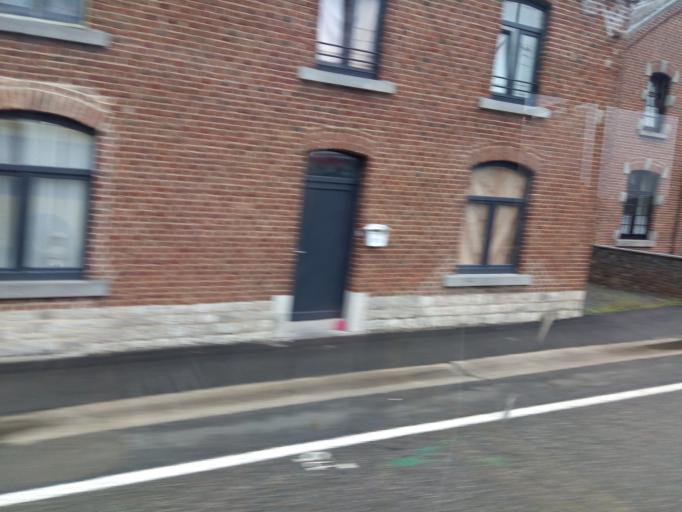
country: BE
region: Wallonia
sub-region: Province du Luxembourg
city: Hotton
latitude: 50.2743
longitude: 5.4392
